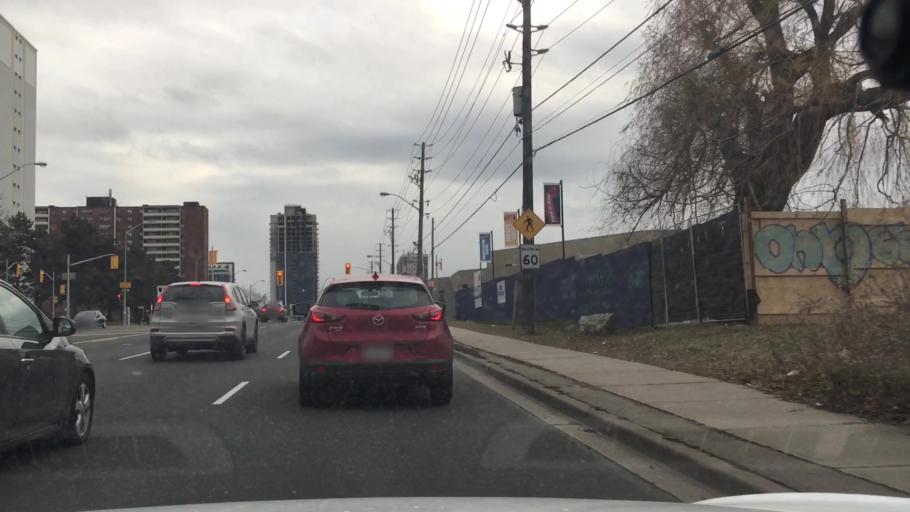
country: CA
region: Ontario
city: Scarborough
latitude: 43.7803
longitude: -79.2334
